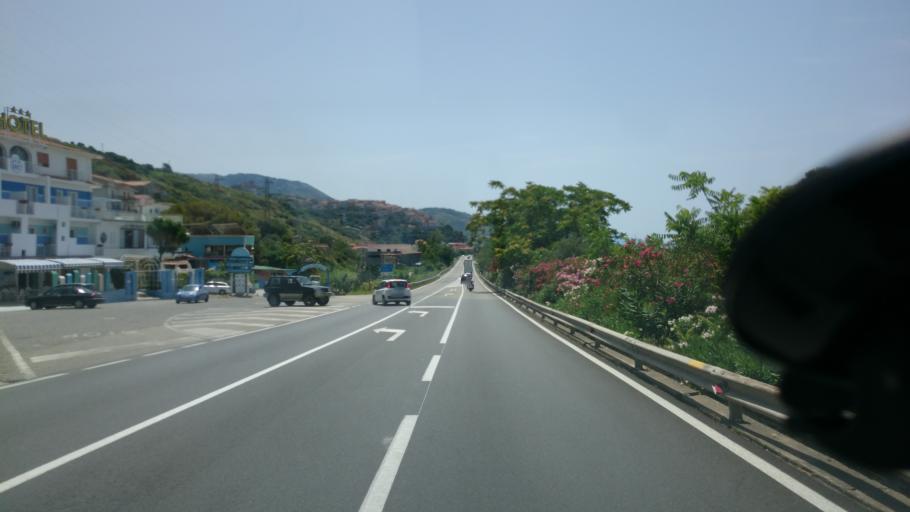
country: IT
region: Calabria
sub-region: Provincia di Cosenza
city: Cetraro Marina
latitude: 39.5288
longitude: 15.9260
